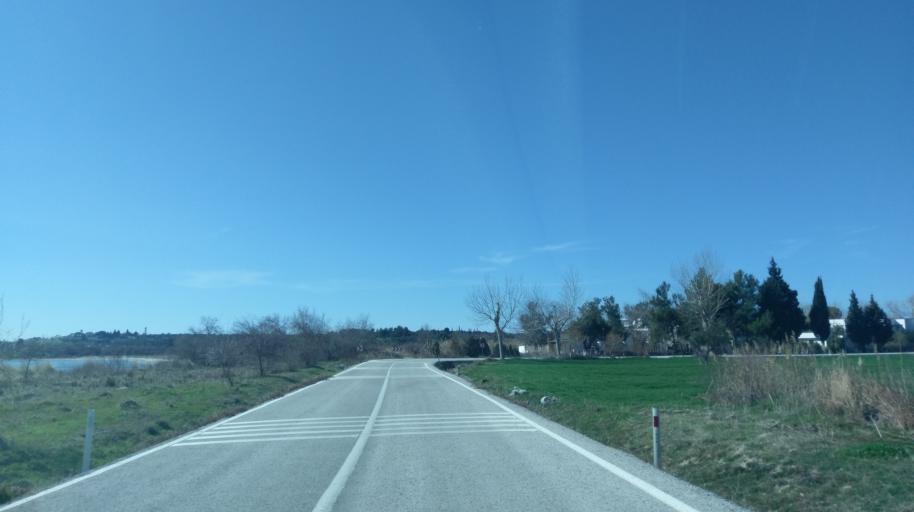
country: TR
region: Canakkale
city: Intepe
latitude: 40.0540
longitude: 26.2064
